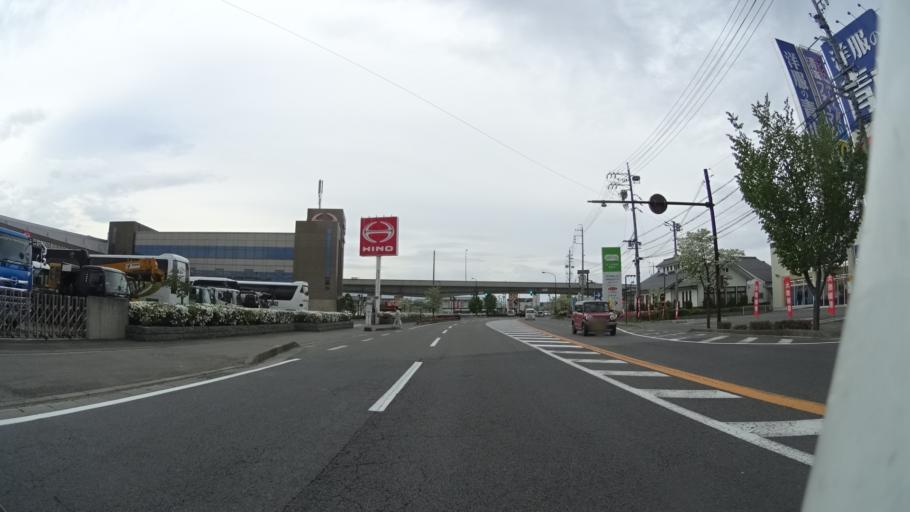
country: JP
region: Nagano
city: Nagano-shi
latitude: 36.6034
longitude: 138.1611
